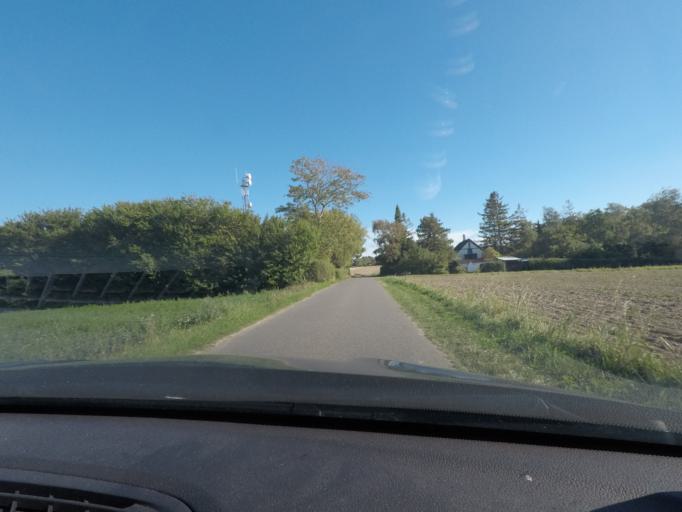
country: DK
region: Zealand
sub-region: Lolland Kommune
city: Maribo
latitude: 54.9758
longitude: 11.5250
